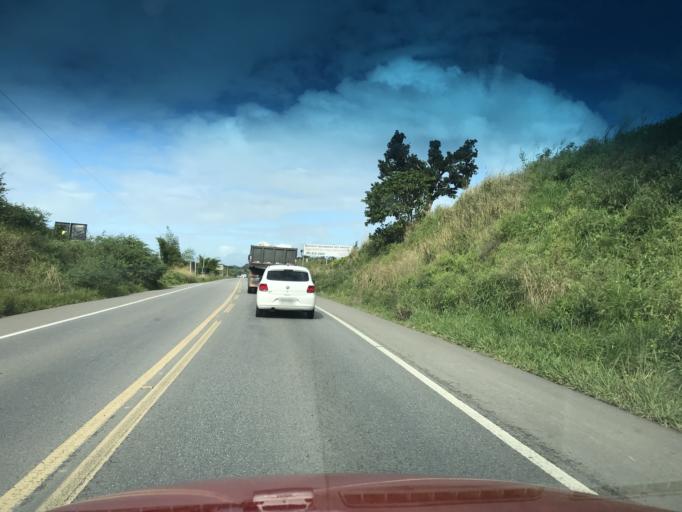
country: BR
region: Bahia
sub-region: Conceicao Do Almeida
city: Muritiba
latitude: -12.8970
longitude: -39.2350
